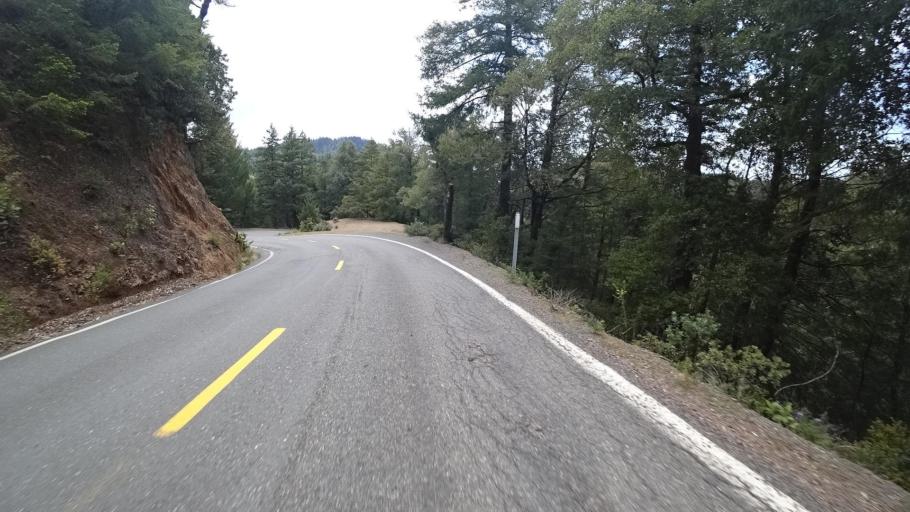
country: US
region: California
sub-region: Humboldt County
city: Redway
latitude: 40.0403
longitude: -124.0230
